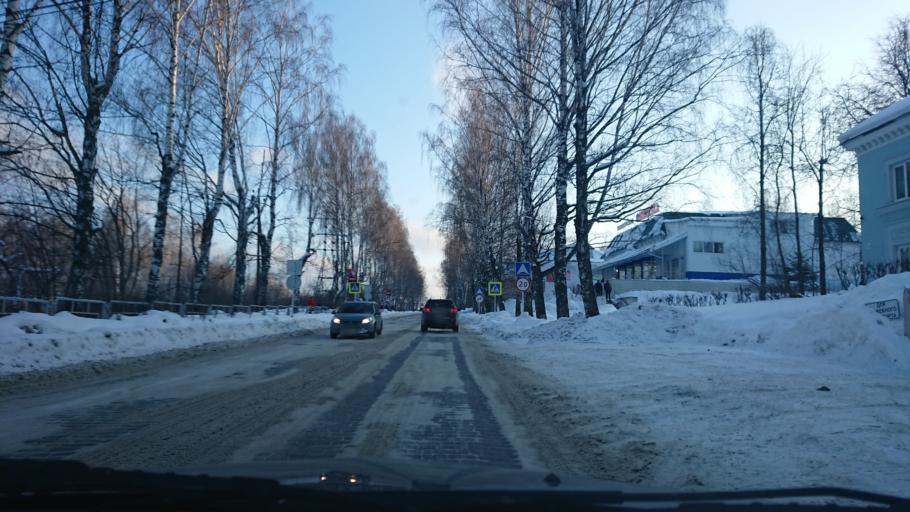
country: RU
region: Sverdlovsk
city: Degtyarsk
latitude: 56.6960
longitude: 60.0883
